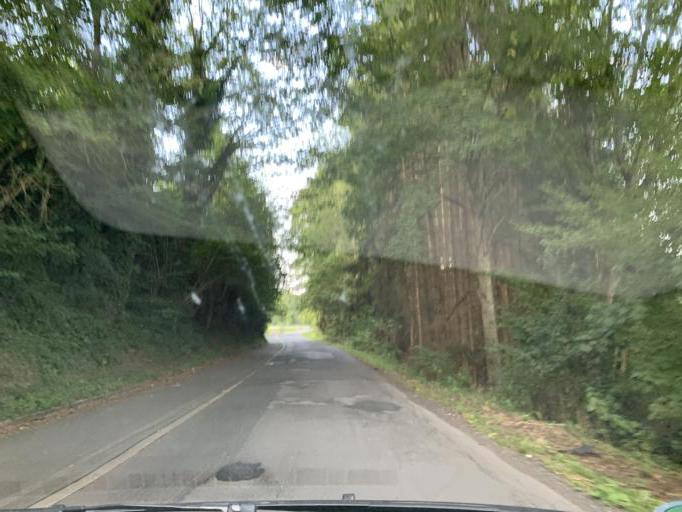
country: DE
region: North Rhine-Westphalia
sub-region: Regierungsbezirk Koln
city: Simmerath
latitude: 50.6178
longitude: 6.3736
